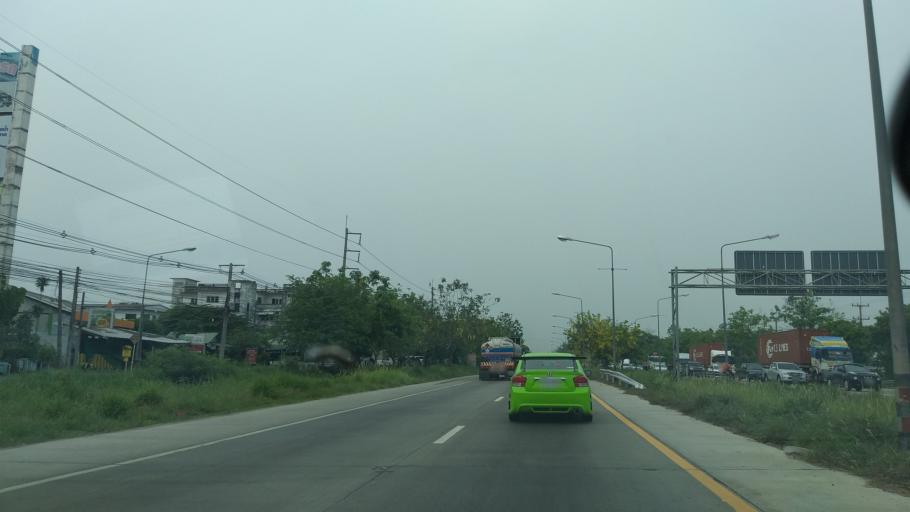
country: TH
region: Chon Buri
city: Ko Chan
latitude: 13.3882
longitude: 101.2792
